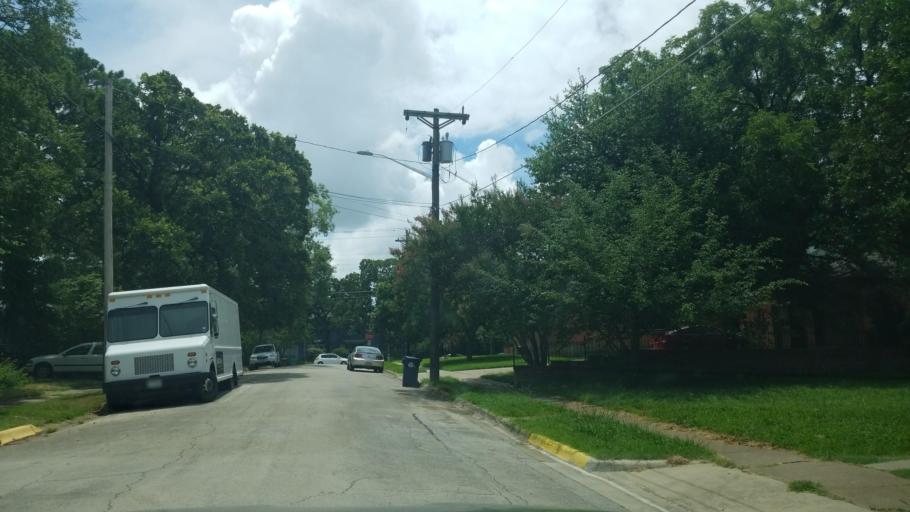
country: US
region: Texas
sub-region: Denton County
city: Denton
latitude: 33.2164
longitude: -97.1519
